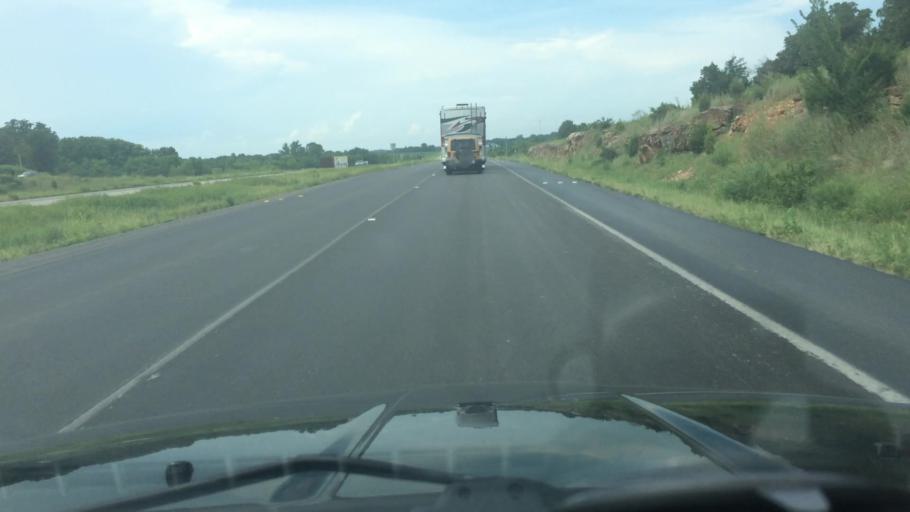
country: US
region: Missouri
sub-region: Saint Clair County
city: Osceola
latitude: 37.9809
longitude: -93.6492
